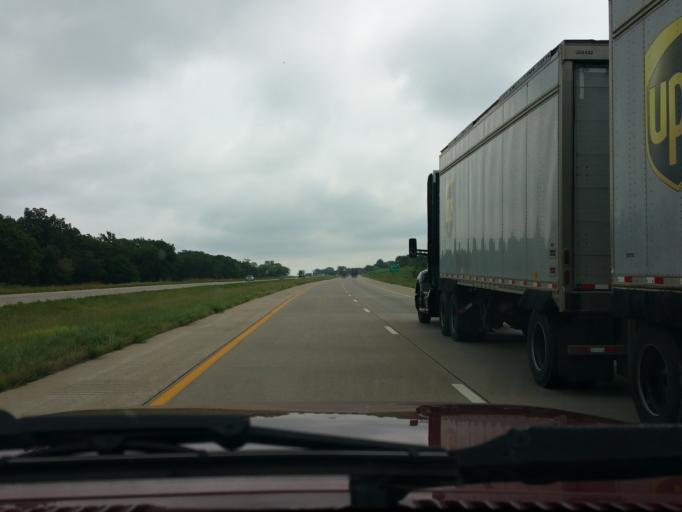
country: US
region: Kansas
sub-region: Shawnee County
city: Silver Lake
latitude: 39.0555
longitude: -95.8404
